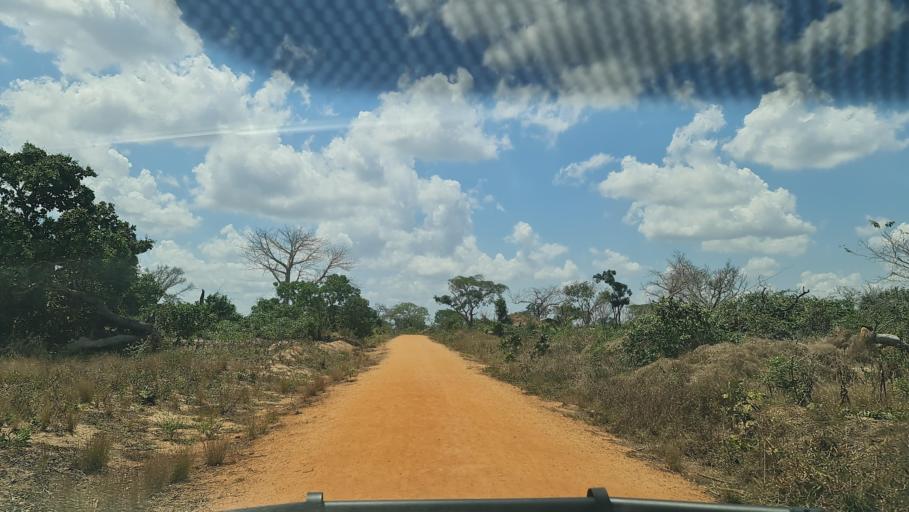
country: MZ
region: Nampula
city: Ilha de Mocambique
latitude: -15.0527
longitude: 40.3292
